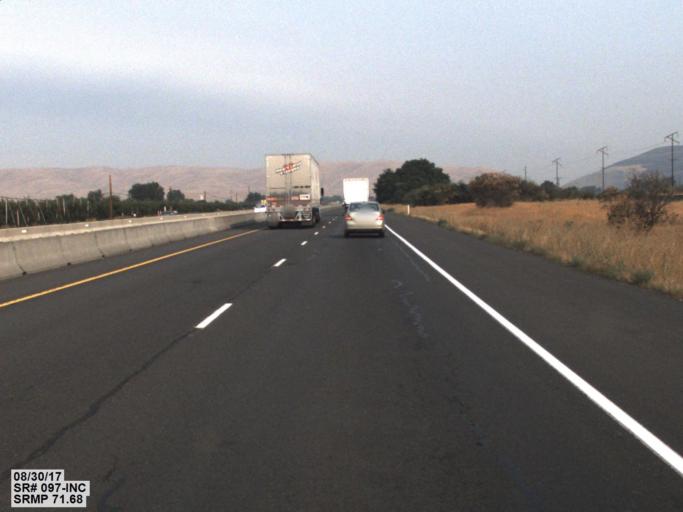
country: US
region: Washington
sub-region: Yakima County
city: Wapato
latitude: 46.4821
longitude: -120.4503
